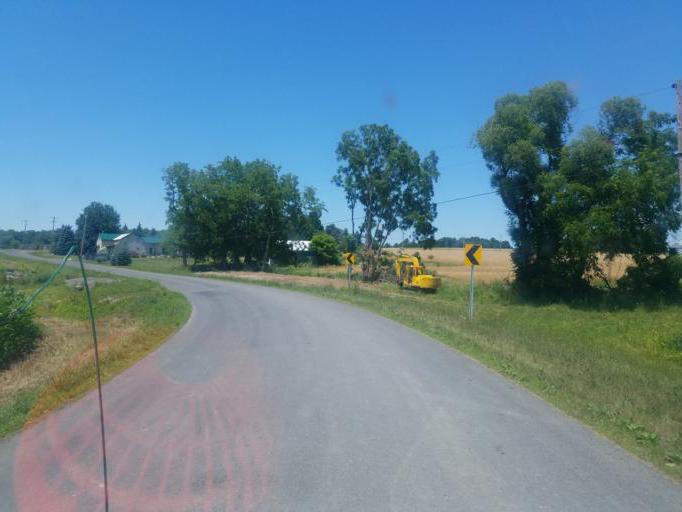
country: US
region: New York
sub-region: Yates County
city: Penn Yan
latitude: 42.6694
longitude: -77.0264
